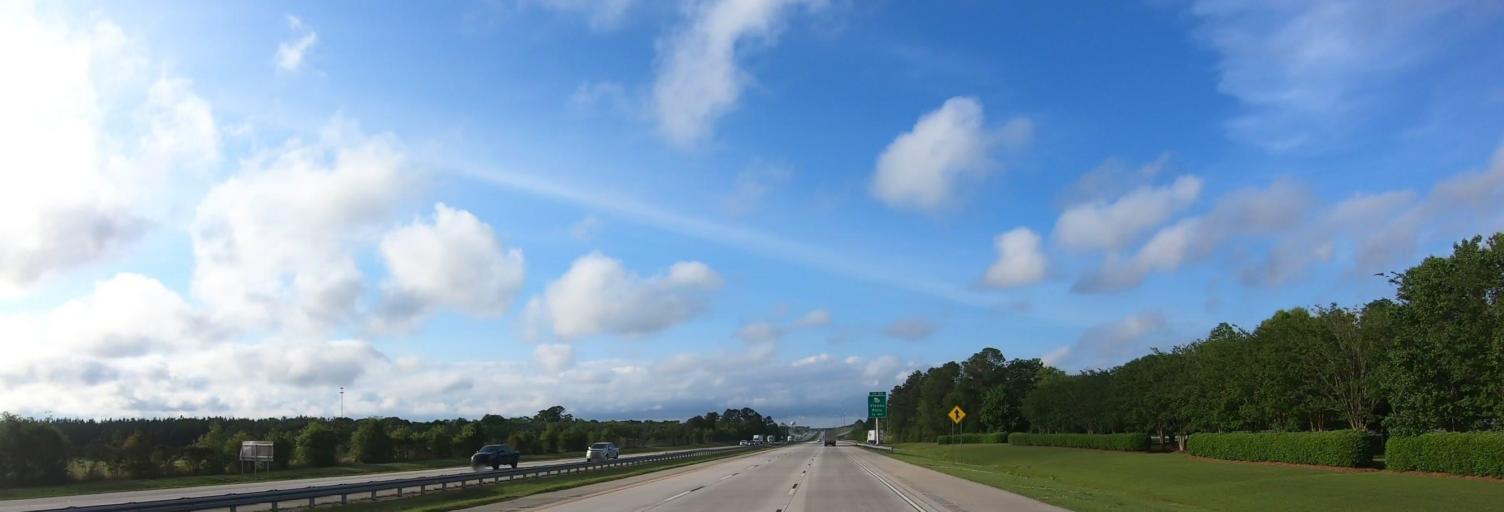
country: US
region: Georgia
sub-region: Dooly County
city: Vienna
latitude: 32.0725
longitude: -83.7625
